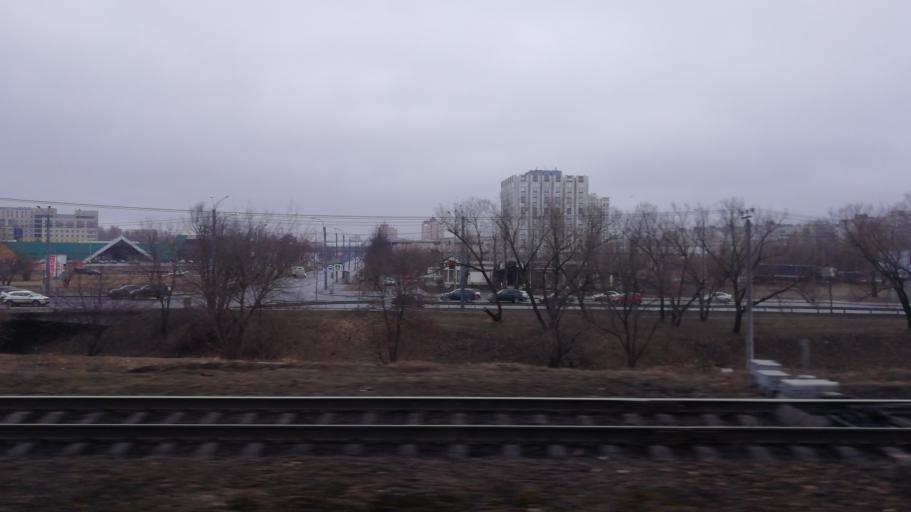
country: RU
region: St.-Petersburg
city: Kupchino
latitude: 59.8735
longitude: 30.3545
